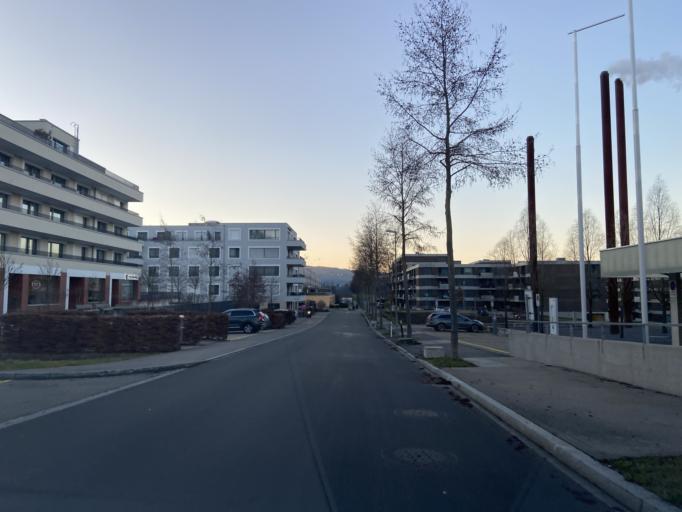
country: CH
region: Zurich
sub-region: Bezirk Winterthur
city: Wuelflingen (Kreis 6) / Niederfeld
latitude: 47.5070
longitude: 8.6813
